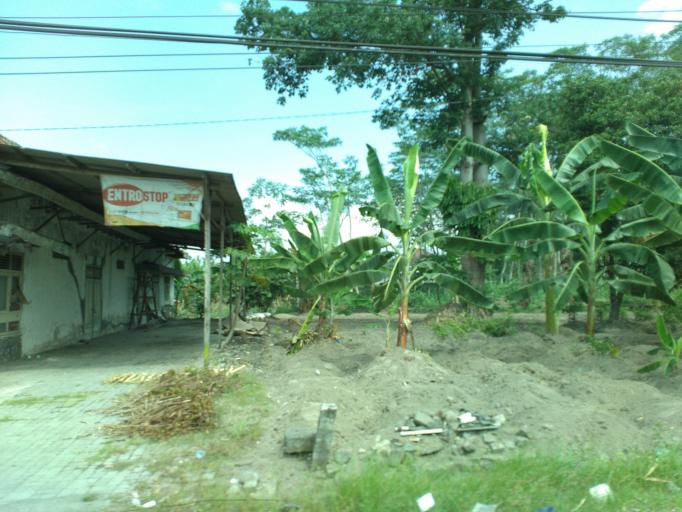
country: ID
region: Central Java
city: Candi Prambanan
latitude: -7.7495
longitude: 110.5213
